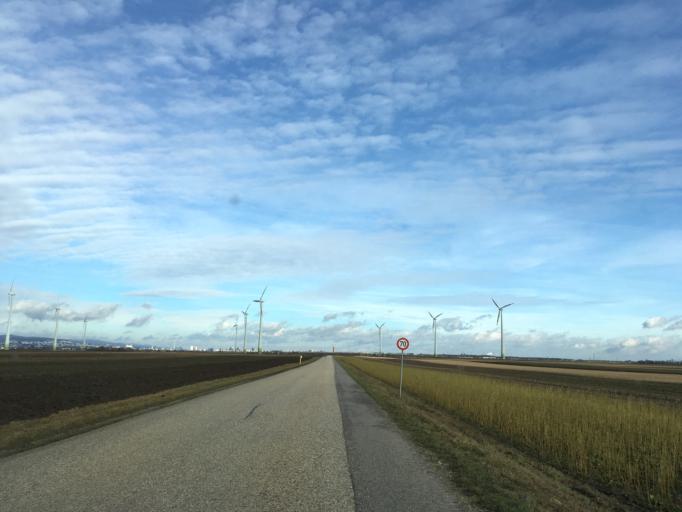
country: AT
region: Burgenland
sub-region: Politischer Bezirk Neusiedl am See
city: Pama
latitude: 48.0603
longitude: 17.0420
